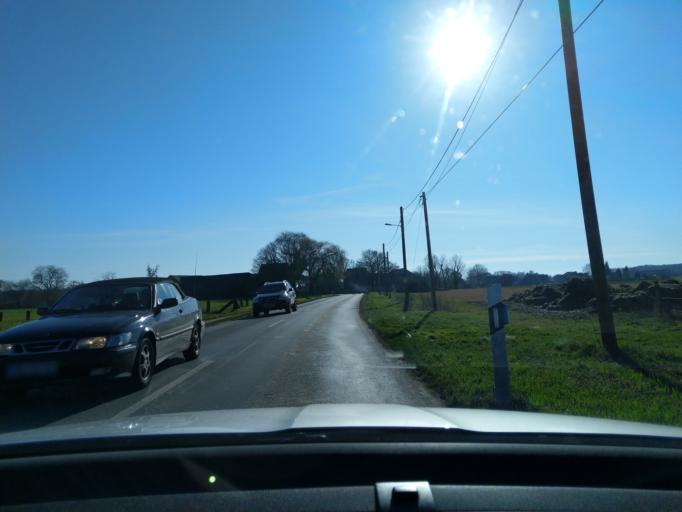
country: DE
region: North Rhine-Westphalia
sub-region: Regierungsbezirk Dusseldorf
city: Monchengladbach
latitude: 51.1405
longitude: 6.3749
